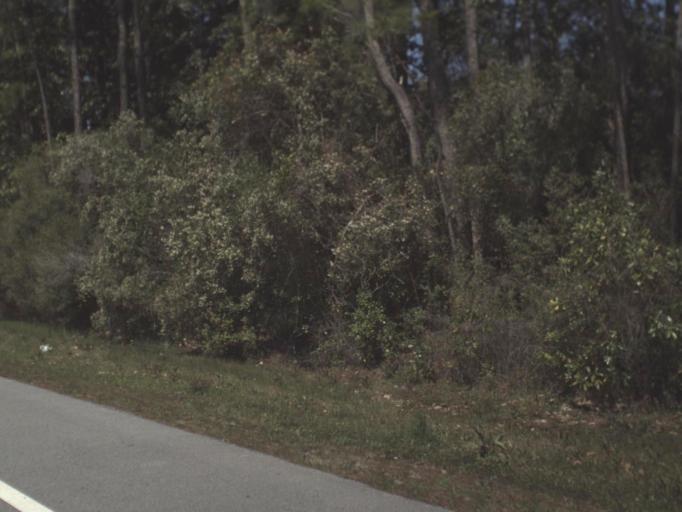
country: US
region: Florida
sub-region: Gulf County
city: Port Saint Joe
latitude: 29.7766
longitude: -85.2884
